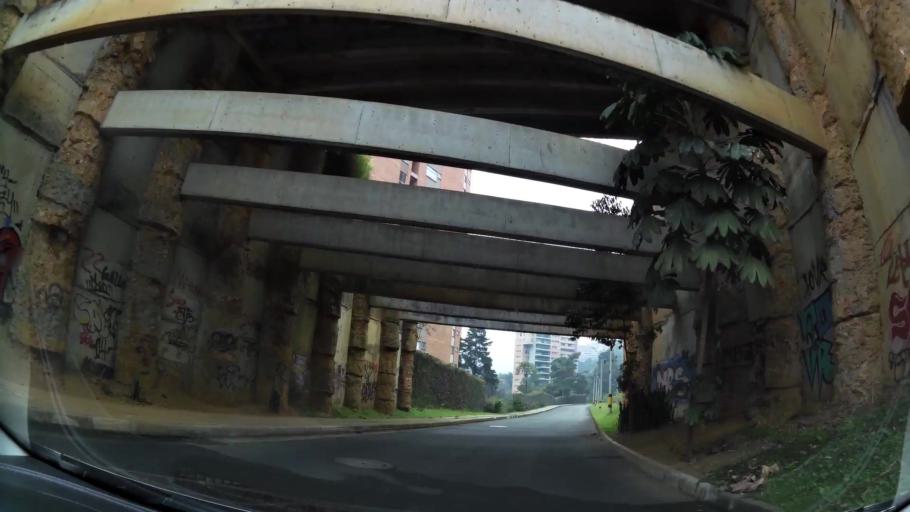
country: CO
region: Antioquia
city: Envigado
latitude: 6.2013
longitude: -75.5542
